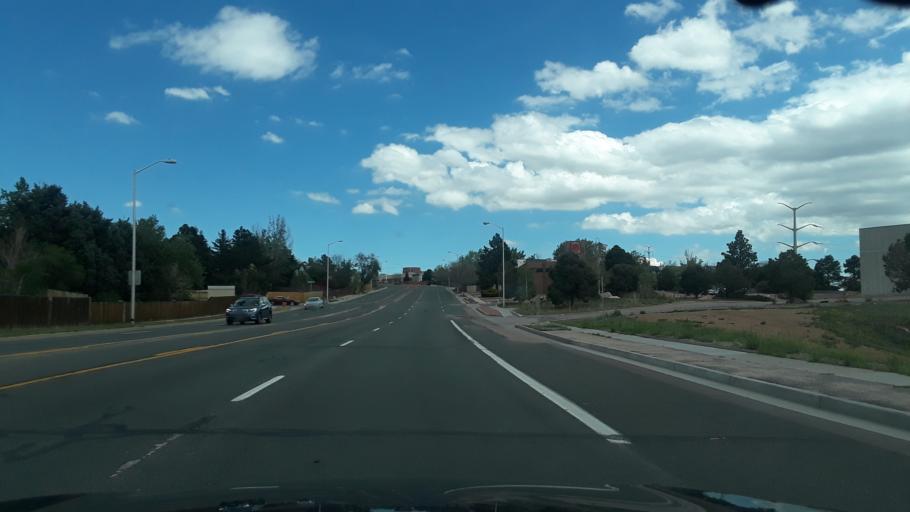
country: US
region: Colorado
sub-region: El Paso County
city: Air Force Academy
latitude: 38.9438
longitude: -104.7823
